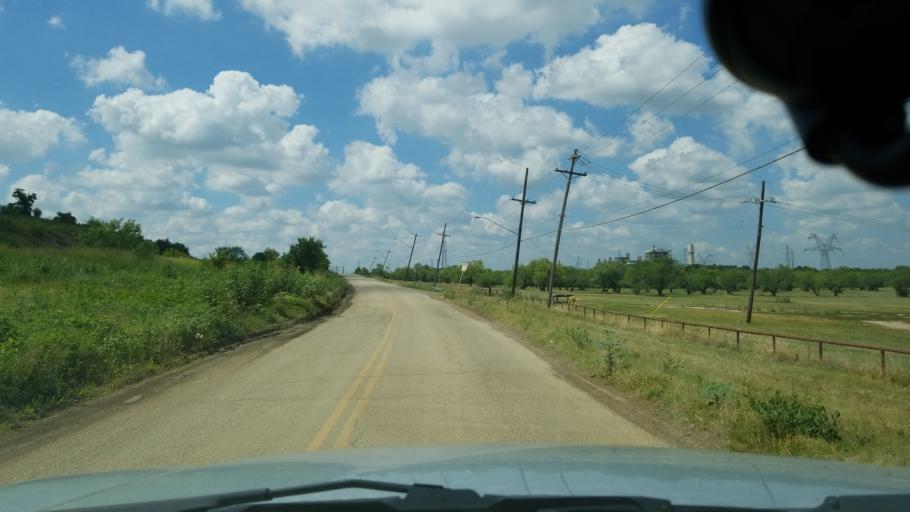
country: US
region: Texas
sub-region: Dallas County
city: Cockrell Hill
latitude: 32.7347
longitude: -96.9308
